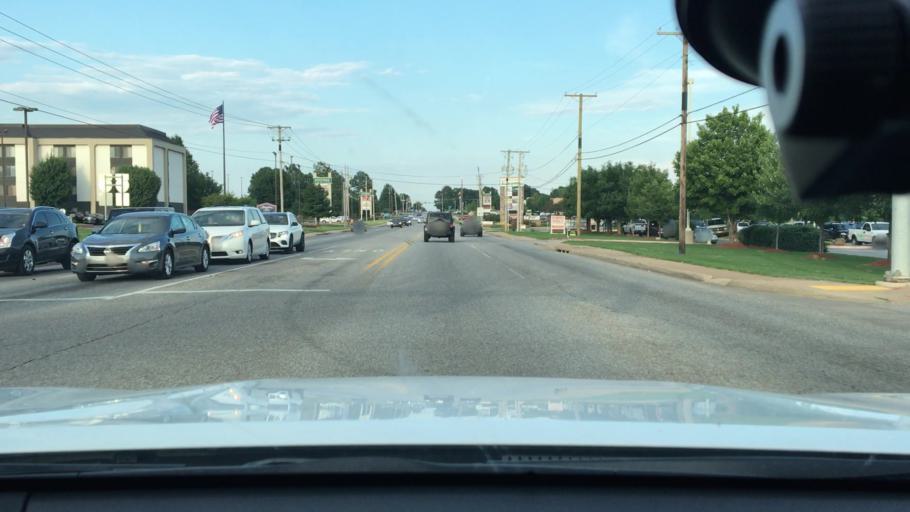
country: US
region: Arkansas
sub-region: Benton County
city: Bentonville
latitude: 36.3349
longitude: -94.1808
